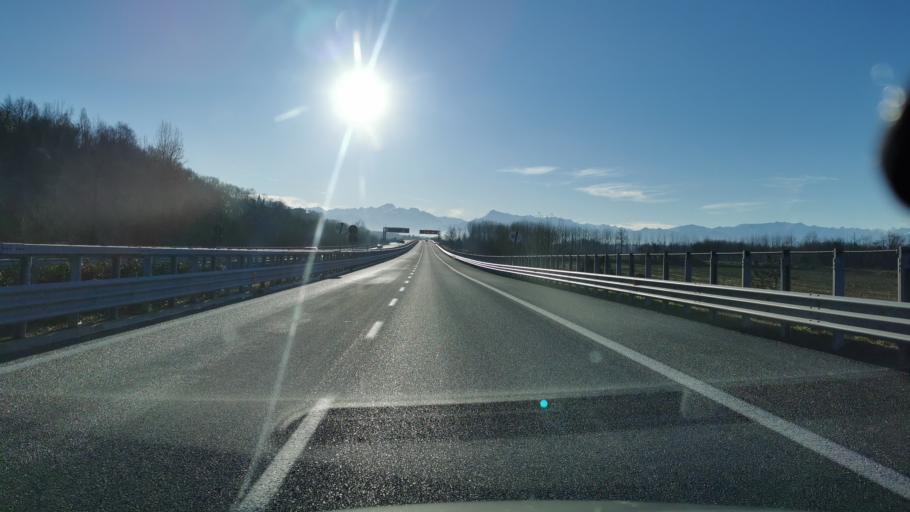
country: IT
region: Piedmont
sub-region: Provincia di Cuneo
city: Montanera
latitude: 44.4729
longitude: 7.6748
